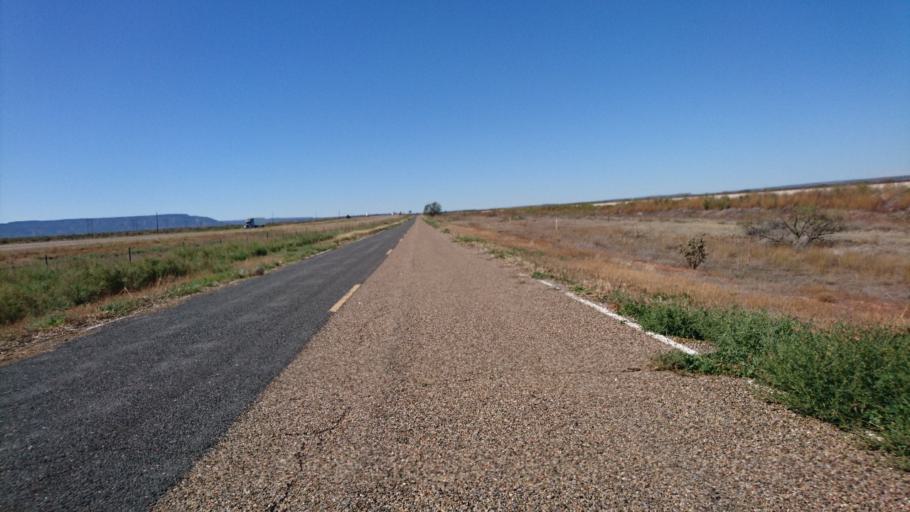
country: US
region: New Mexico
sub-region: Quay County
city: Tucumcari
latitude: 35.1030
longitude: -104.0394
